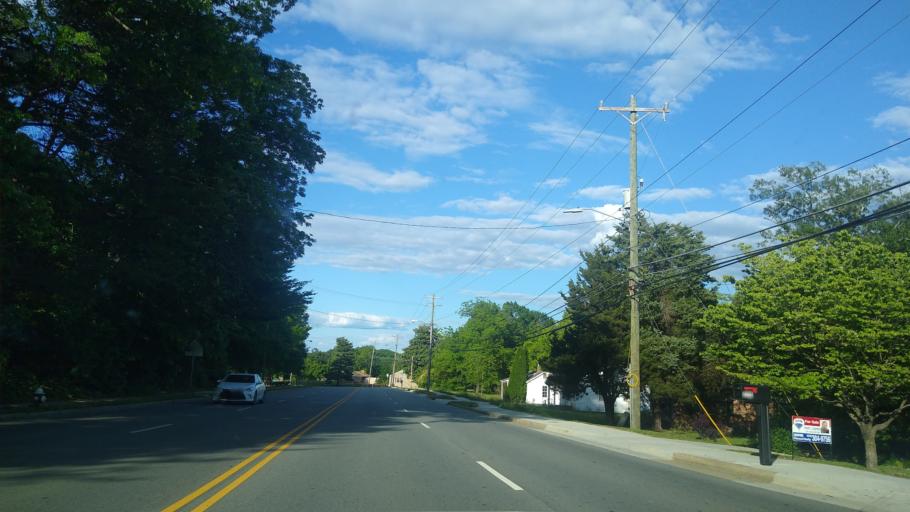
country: US
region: North Carolina
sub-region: Guilford County
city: Greensboro
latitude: 36.1402
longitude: -79.7744
